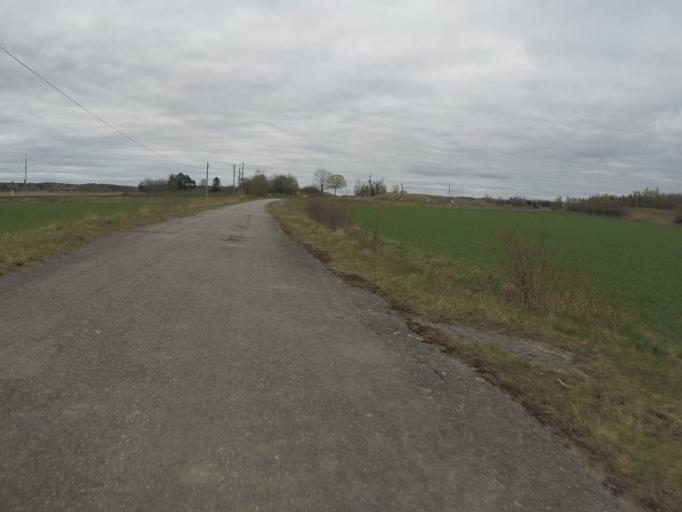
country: SE
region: Soedermanland
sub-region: Eskilstuna Kommun
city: Hallbybrunn
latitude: 59.4081
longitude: 16.4015
